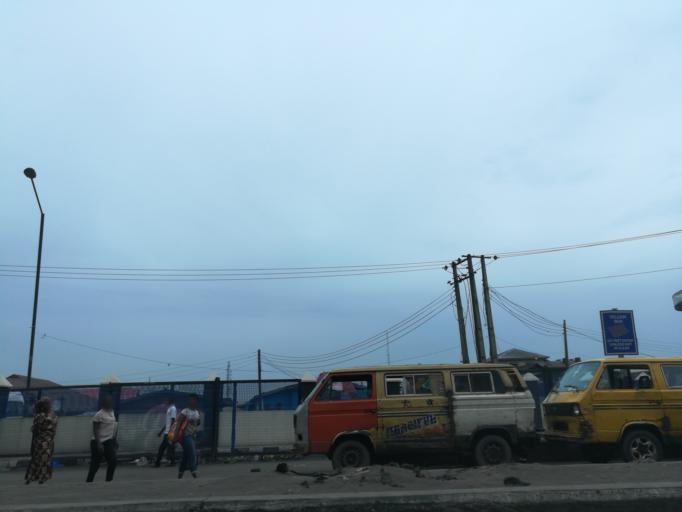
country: NG
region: Lagos
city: Ebute Metta
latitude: 6.4794
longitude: 3.3832
